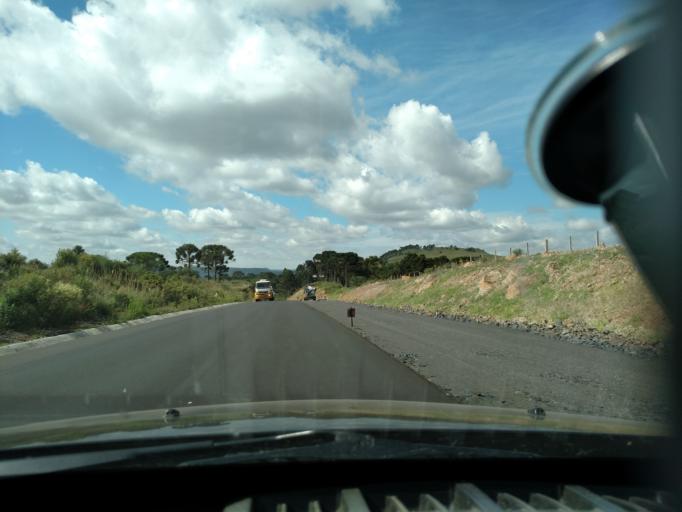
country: BR
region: Santa Catarina
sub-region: Sao Joaquim
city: Sao Joaquim
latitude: -28.0732
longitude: -50.0728
